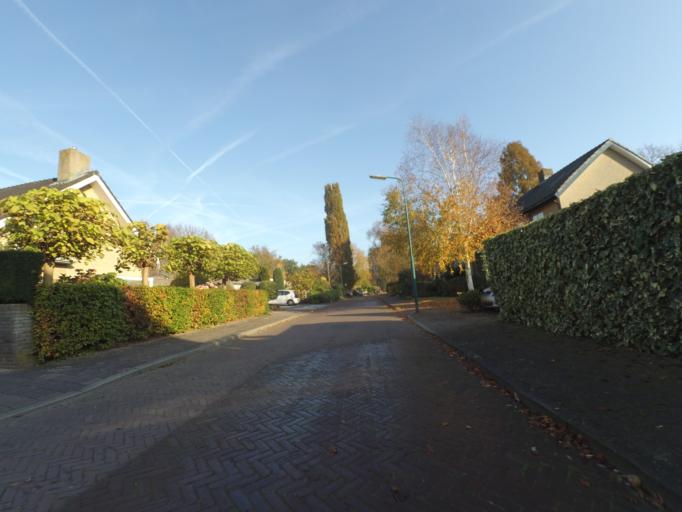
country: NL
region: Utrecht
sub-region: Gemeente Leusden
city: Leusden
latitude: 52.1385
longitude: 5.4309
